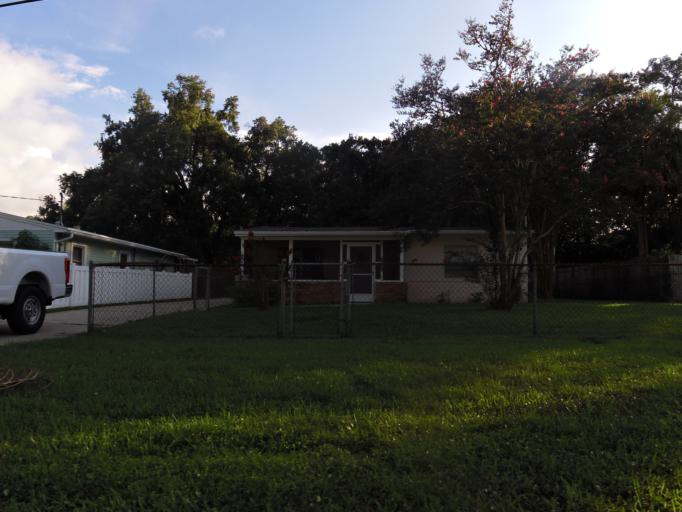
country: US
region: Florida
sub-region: Duval County
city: Jacksonville
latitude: 30.2969
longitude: -81.6268
